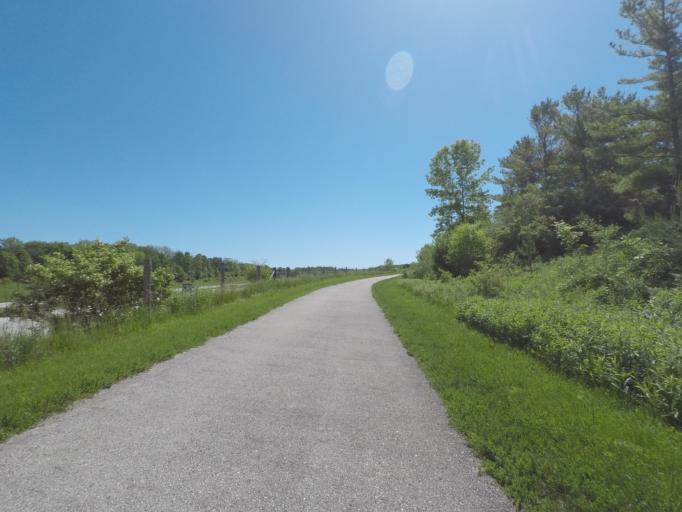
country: US
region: Wisconsin
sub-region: Sheboygan County
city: Kohler
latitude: 43.7531
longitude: -87.7842
